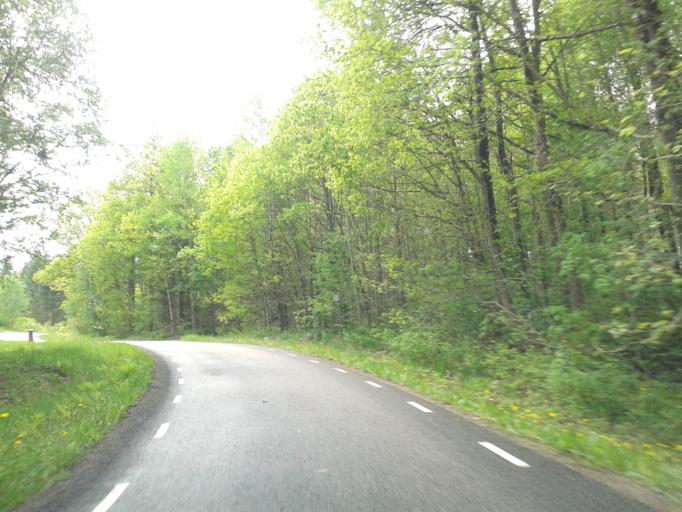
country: SE
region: Vaestra Goetaland
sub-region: Kungalvs Kommun
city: Kungalv
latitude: 57.9297
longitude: 11.9524
